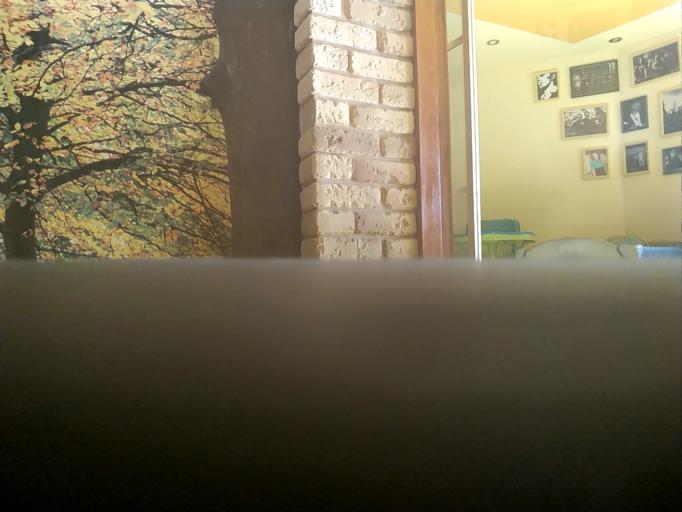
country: RU
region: Smolensk
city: Temkino
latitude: 55.0651
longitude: 34.9129
